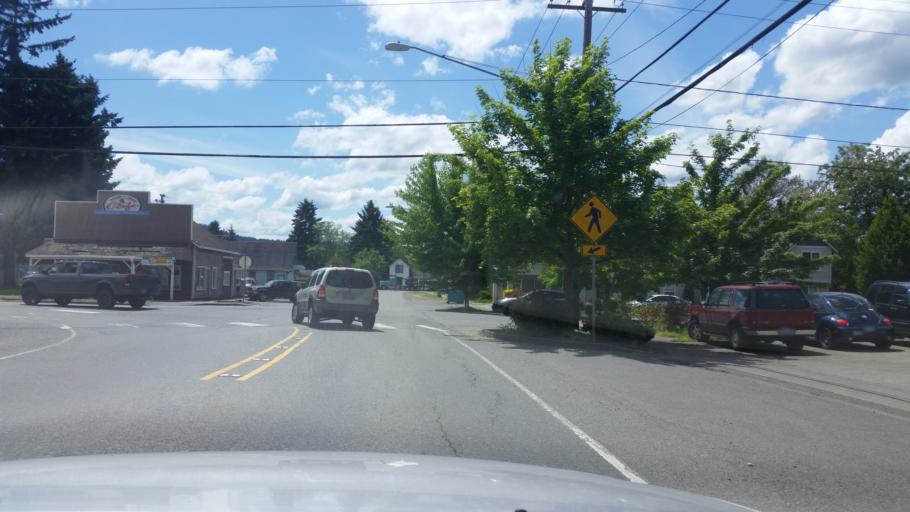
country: US
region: Washington
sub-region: Pierce County
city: Orting
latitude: 47.0955
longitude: -122.2022
